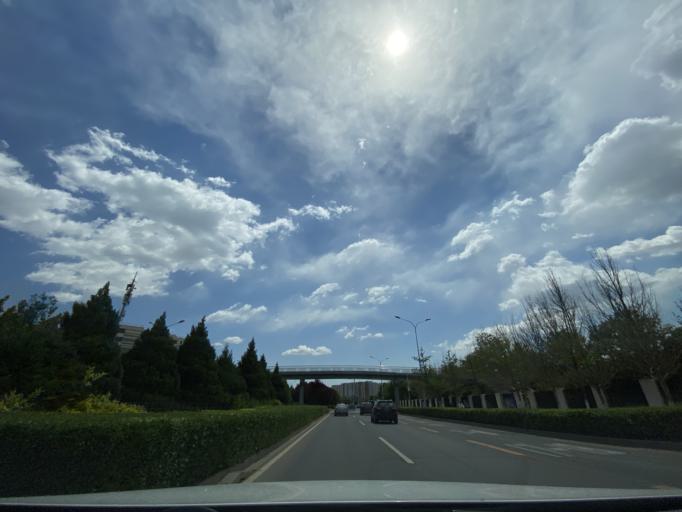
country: CN
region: Beijing
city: Sijiqing
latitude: 39.9357
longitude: 116.2433
